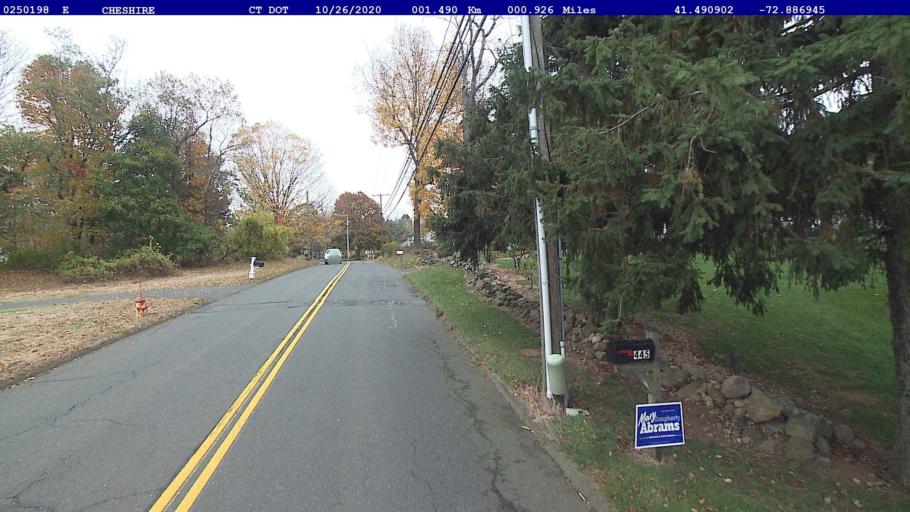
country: US
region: Connecticut
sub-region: New Haven County
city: Cheshire
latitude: 41.4909
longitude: -72.8869
